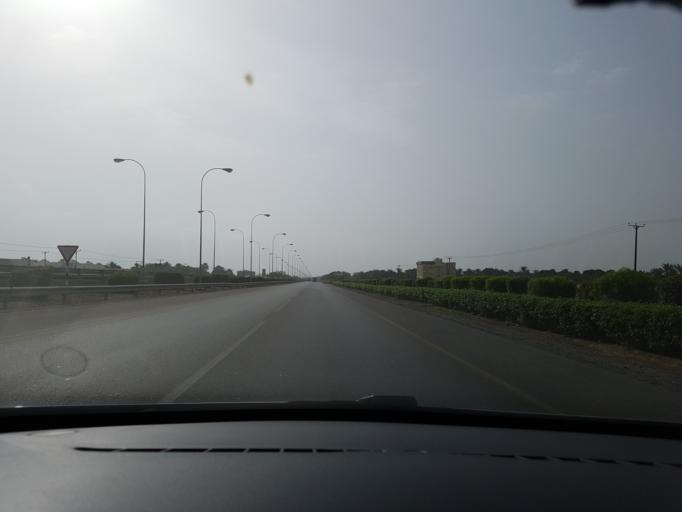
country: OM
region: Al Batinah
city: Al Sohar
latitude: 24.4042
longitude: 56.6564
